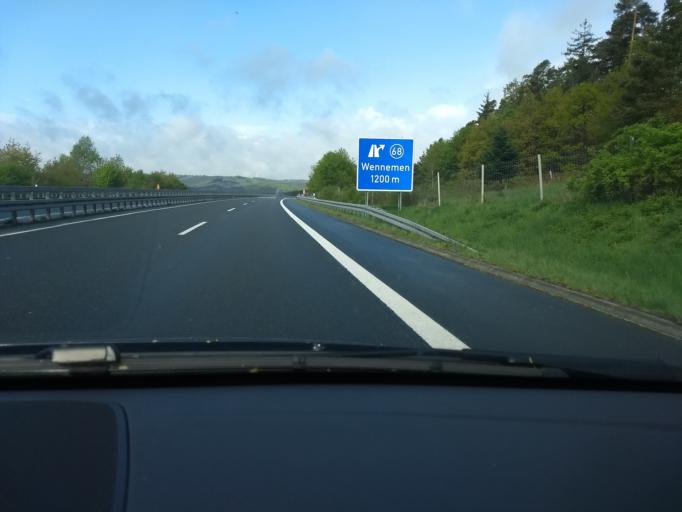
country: DE
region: North Rhine-Westphalia
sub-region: Regierungsbezirk Arnsberg
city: Meschede
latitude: 51.3571
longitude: 8.2107
